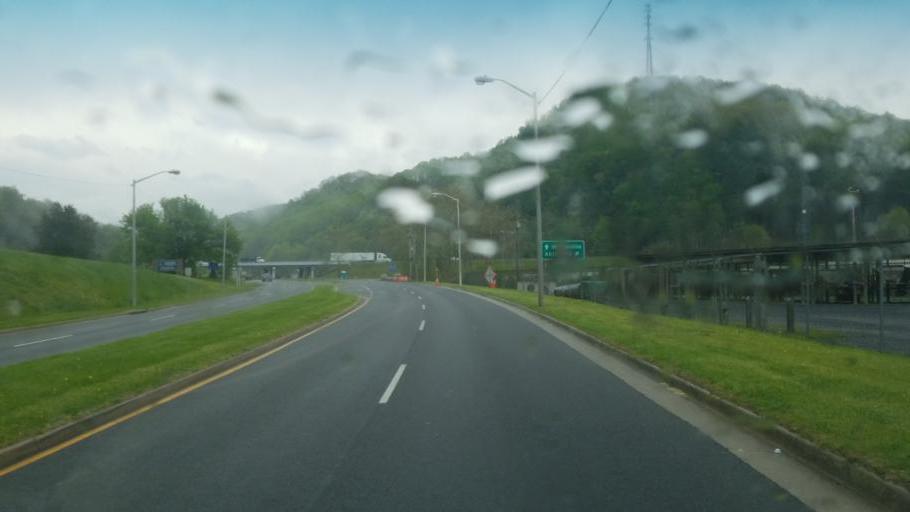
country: US
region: Virginia
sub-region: Smyth County
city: Marion
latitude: 36.8281
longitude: -81.5094
